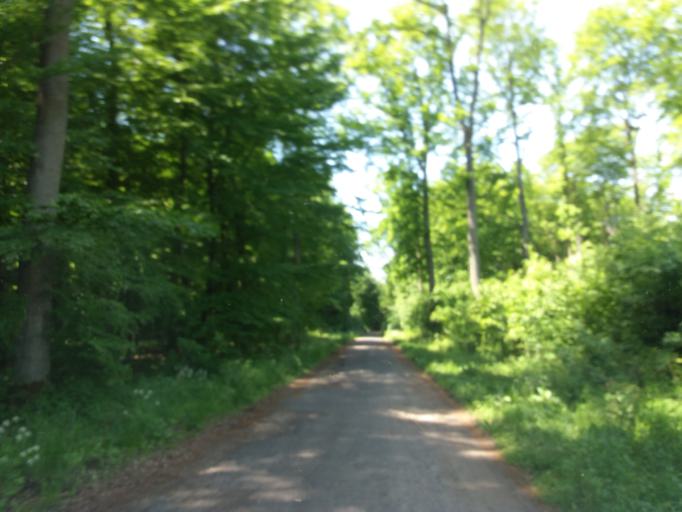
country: PL
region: West Pomeranian Voivodeship
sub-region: Powiat stargardzki
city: Dobrzany
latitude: 53.3471
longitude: 15.4928
